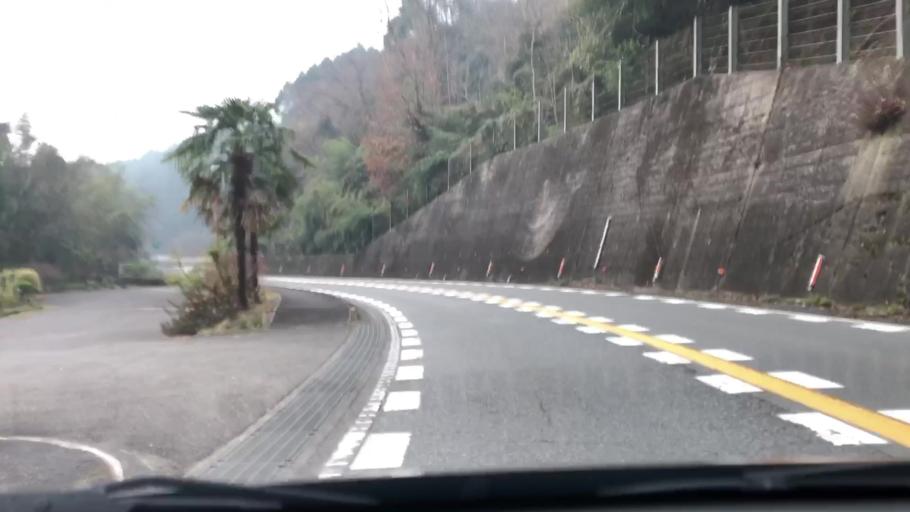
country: JP
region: Oita
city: Usuki
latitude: 33.0247
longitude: 131.6942
